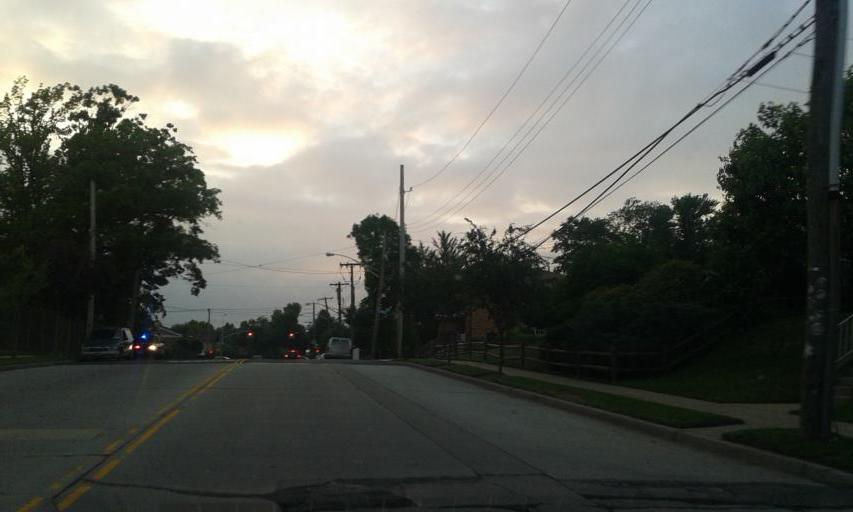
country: US
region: New York
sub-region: Richmond County
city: Staten Island
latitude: 40.5679
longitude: -74.1232
